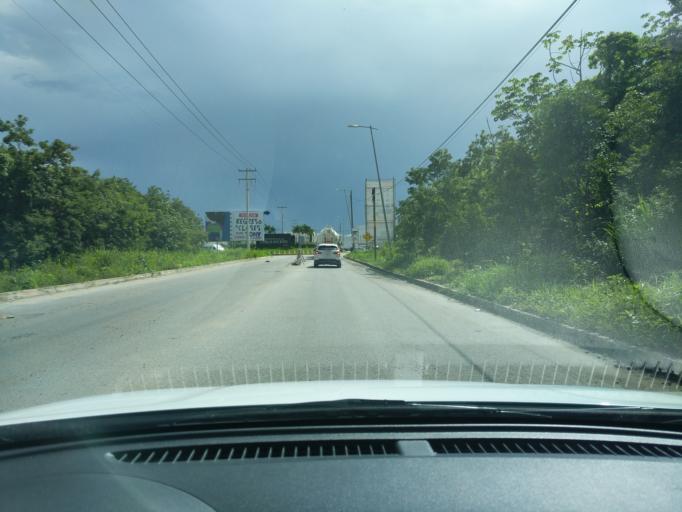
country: MX
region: Quintana Roo
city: Cancun
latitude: 21.1768
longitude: -86.9154
